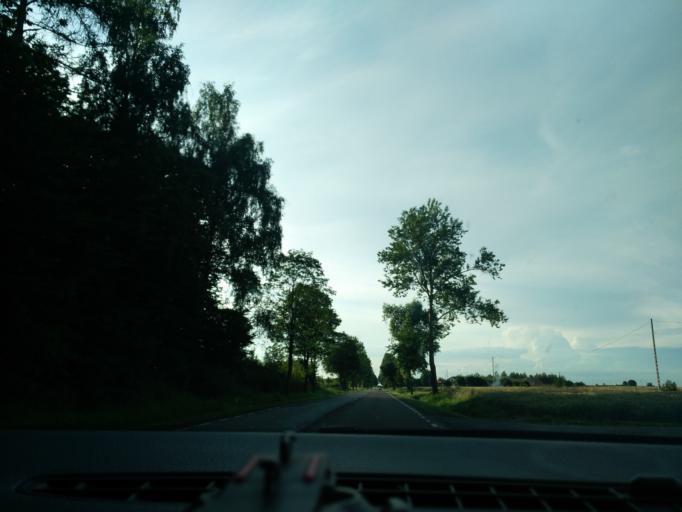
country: PL
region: Lublin Voivodeship
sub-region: Powiat krasnicki
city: Krasnik
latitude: 50.8721
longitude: 22.2698
